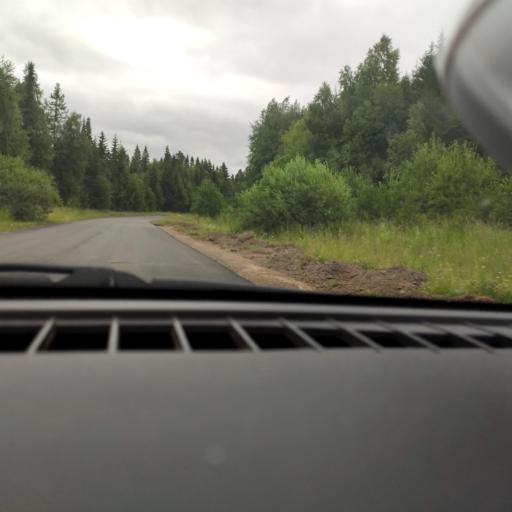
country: RU
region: Perm
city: Polazna
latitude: 58.3405
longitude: 56.2189
